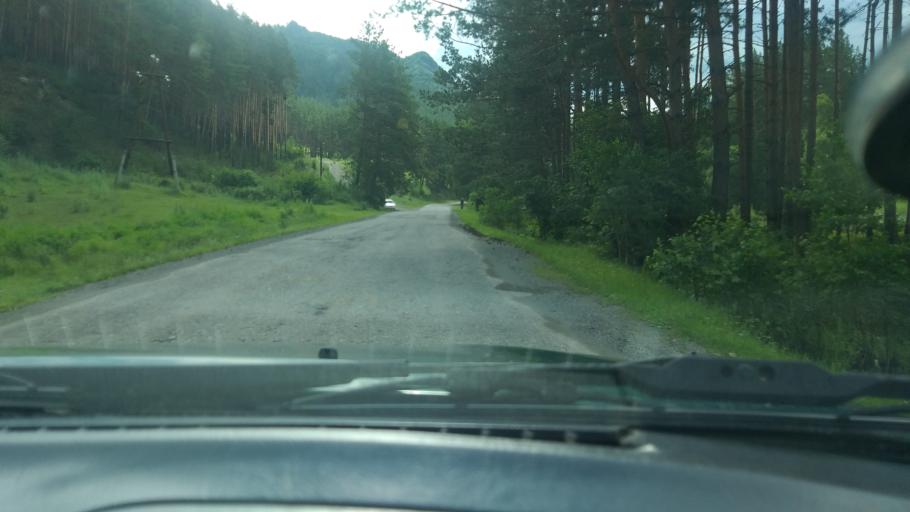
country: RU
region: Altay
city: Chemal
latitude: 51.3914
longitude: 86.0469
